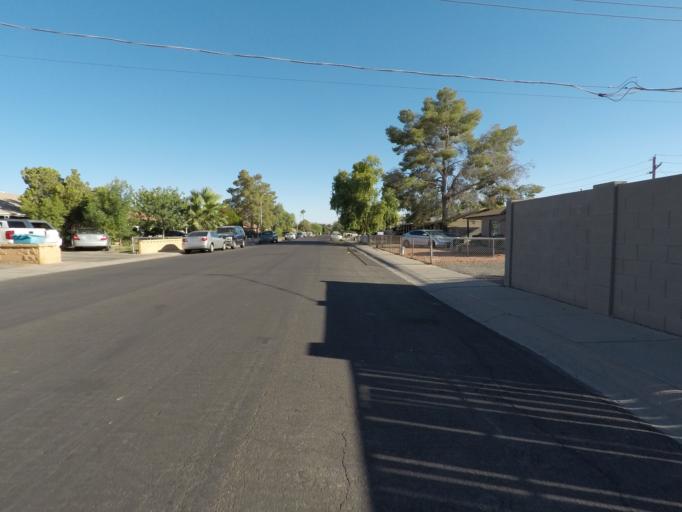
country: US
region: Arizona
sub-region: Maricopa County
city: Glendale
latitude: 33.5194
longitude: -112.1300
